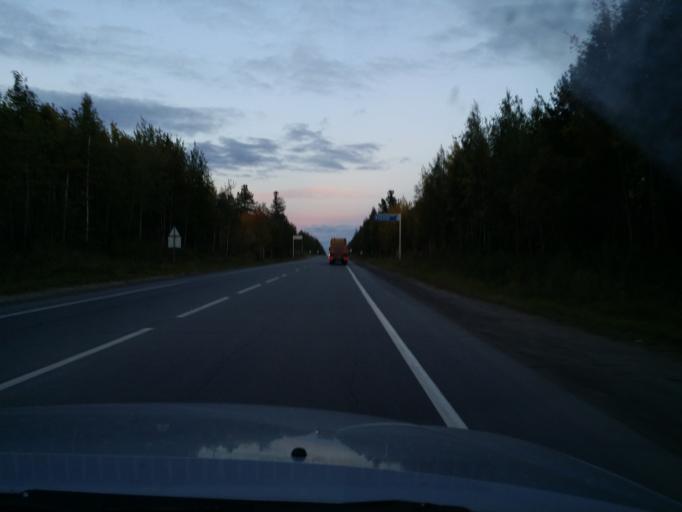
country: RU
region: Khanty-Mansiyskiy Avtonomnyy Okrug
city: Megion
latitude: 61.0589
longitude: 76.2902
